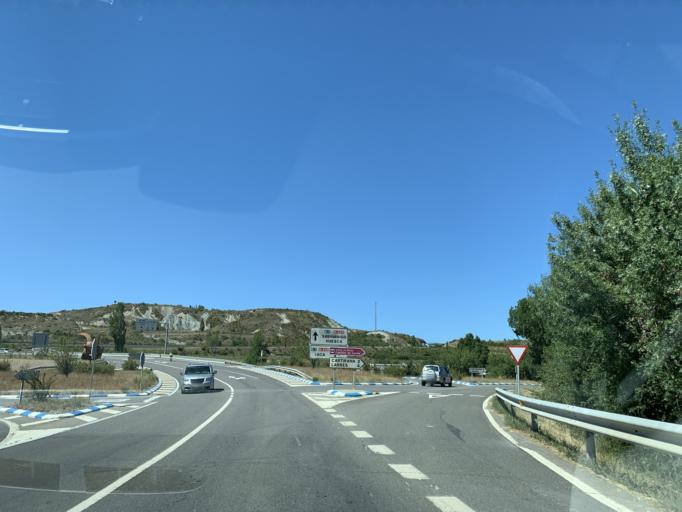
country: ES
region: Aragon
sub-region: Provincia de Huesca
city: Sabinanigo
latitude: 42.5370
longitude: -0.3684
